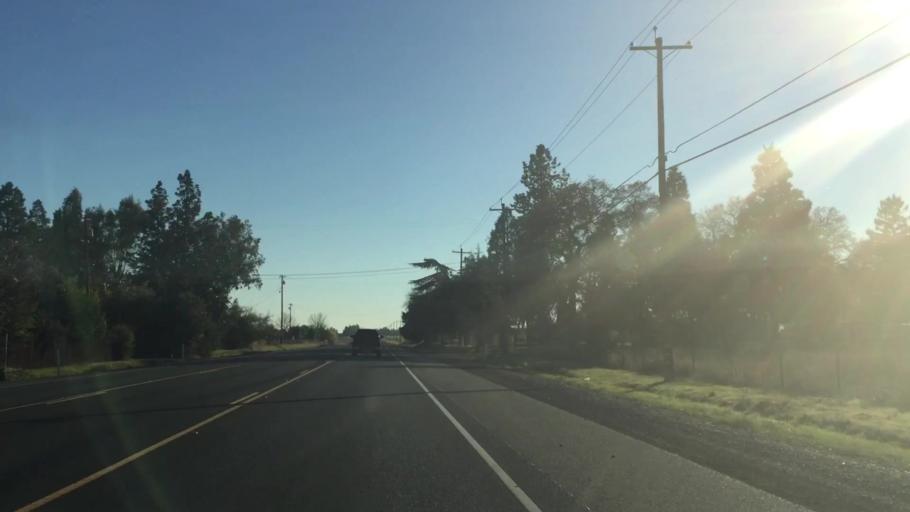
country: US
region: California
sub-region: Butte County
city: Palermo
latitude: 39.4269
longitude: -121.6051
